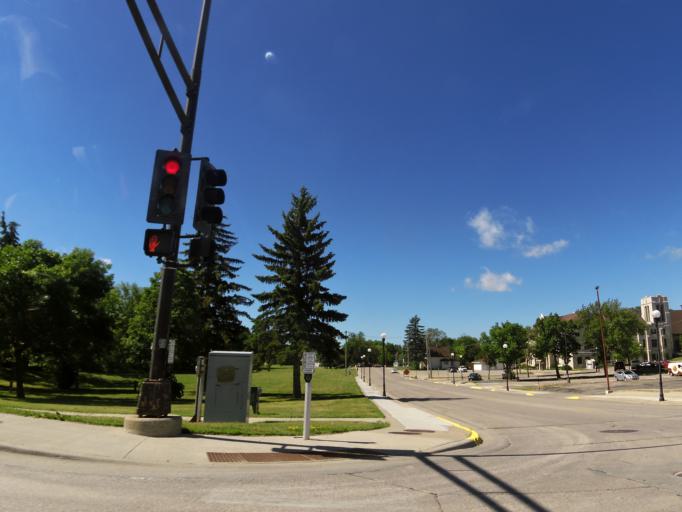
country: US
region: Minnesota
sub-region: Polk County
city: Crookston
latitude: 47.7732
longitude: -96.6055
